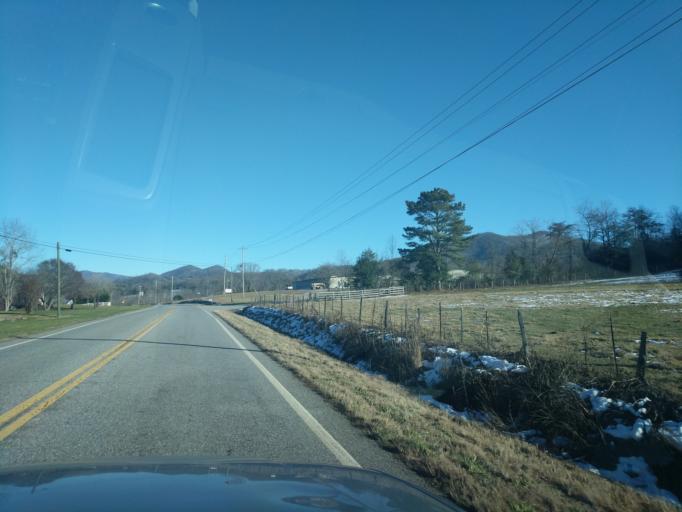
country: US
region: Georgia
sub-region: Towns County
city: Hiawassee
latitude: 34.9183
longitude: -83.7200
